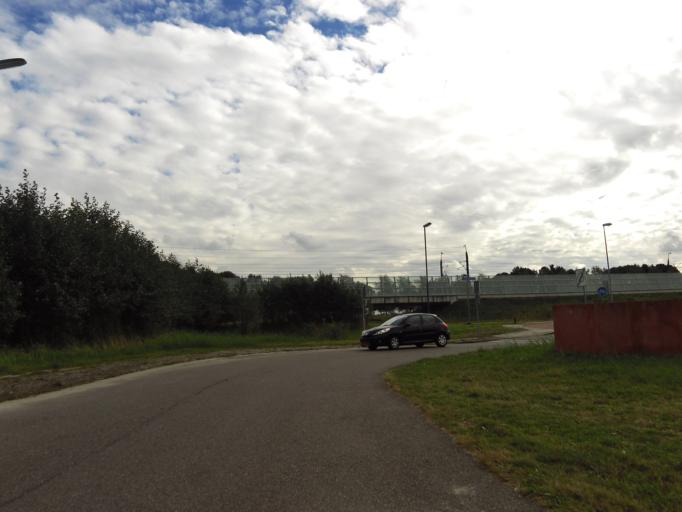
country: NL
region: South Holland
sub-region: Gemeente Rijnwoude
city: Benthuizen
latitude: 52.0620
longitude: 4.5547
